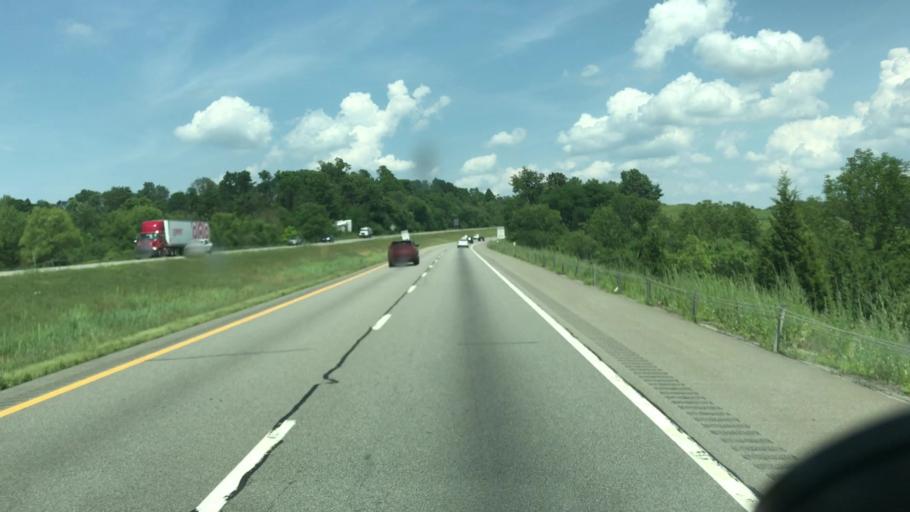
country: US
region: New York
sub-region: Dutchess County
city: Beacon
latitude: 41.5260
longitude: -73.9577
